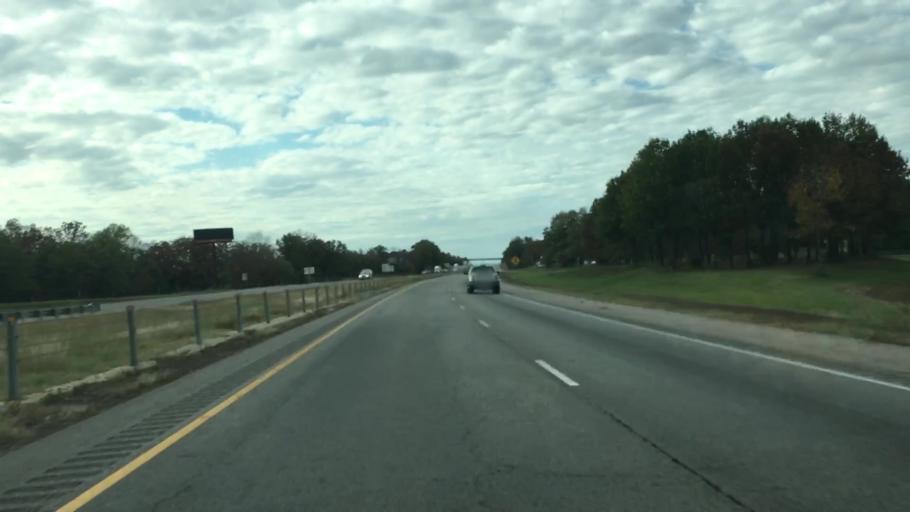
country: US
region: Arkansas
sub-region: Conway County
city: Morrilton
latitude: 35.1754
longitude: -92.7452
